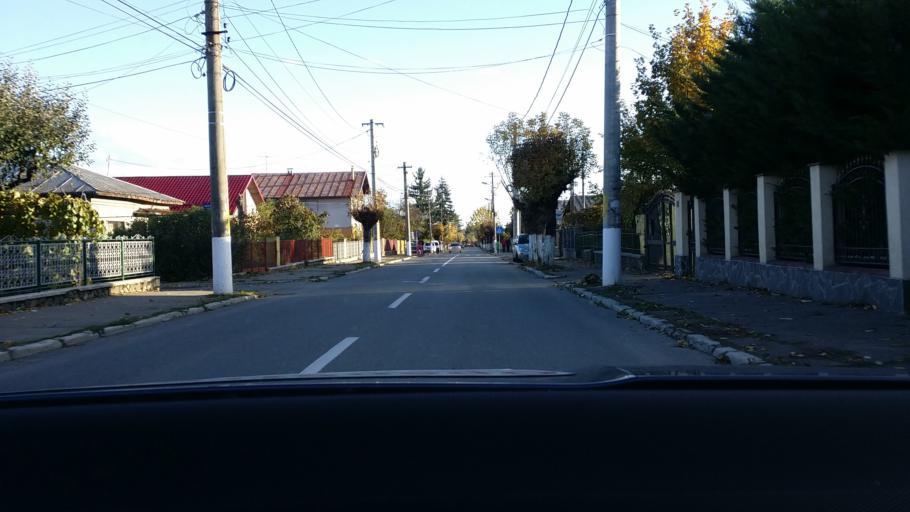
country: RO
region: Prahova
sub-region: Municipiul Campina
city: Campina
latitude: 45.1423
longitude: 25.7338
